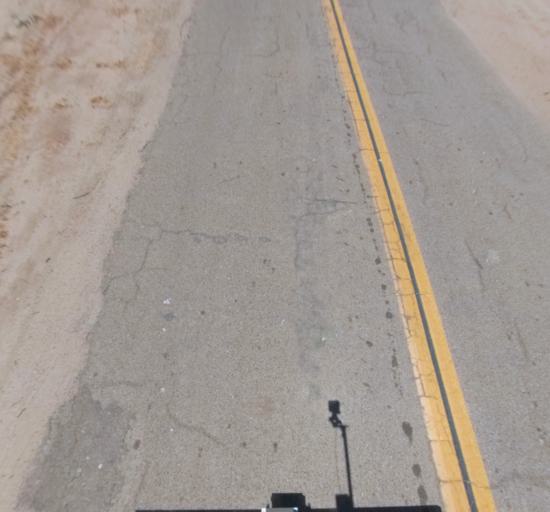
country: US
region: California
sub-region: Madera County
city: Fairmead
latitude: 37.0110
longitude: -120.2746
